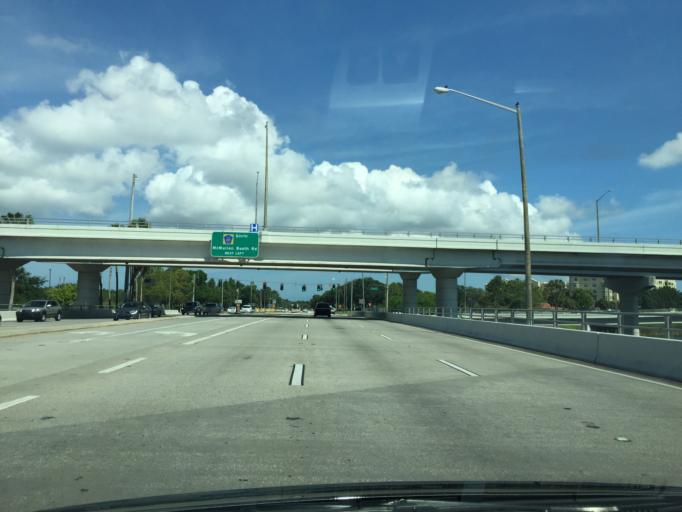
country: US
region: Florida
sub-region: Pinellas County
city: Saint George
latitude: 28.0610
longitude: -82.7103
